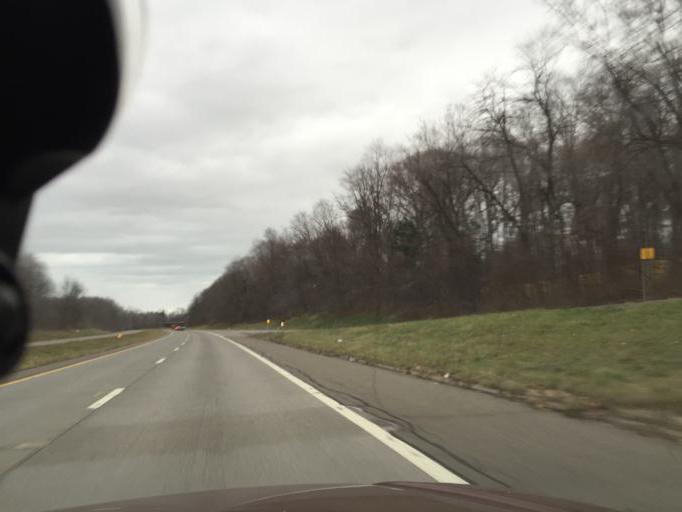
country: US
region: New York
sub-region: Monroe County
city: Greece
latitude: 43.2322
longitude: -77.6718
